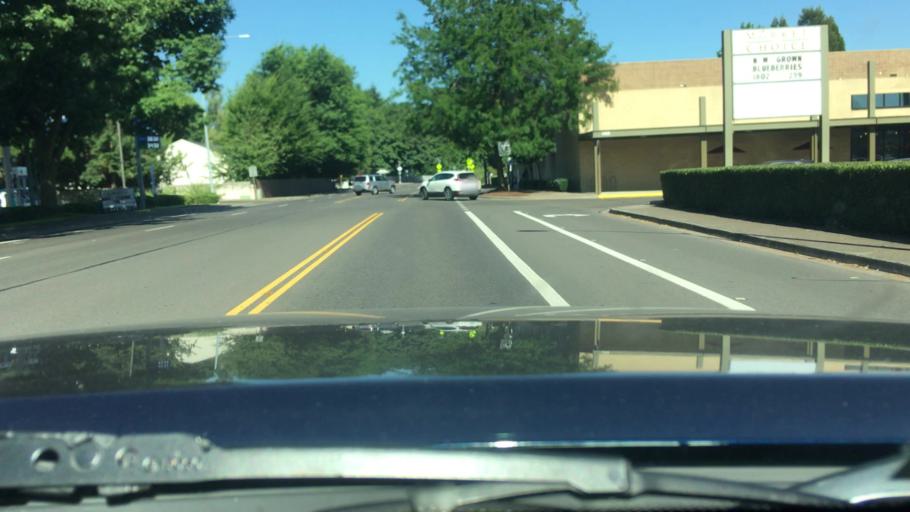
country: US
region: Oregon
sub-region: Lane County
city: Eugene
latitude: 44.0932
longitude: -123.0946
